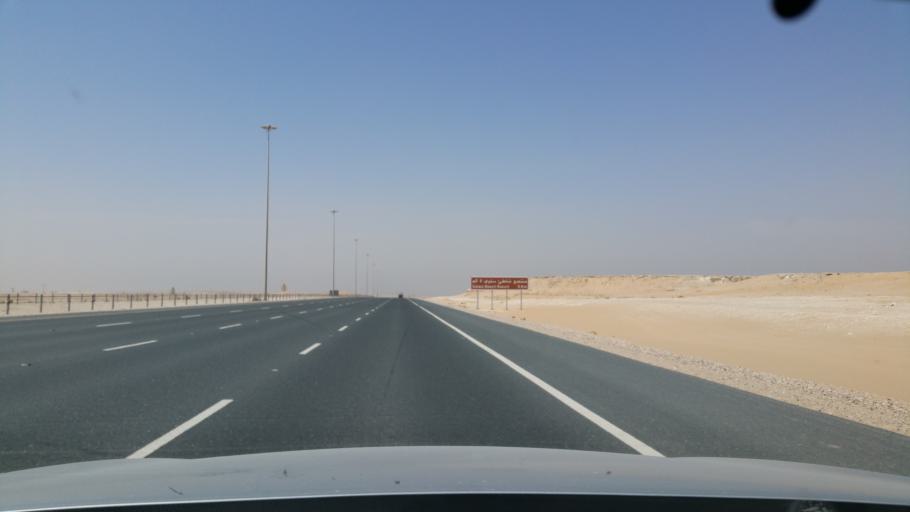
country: QA
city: Umm Bab
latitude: 24.8718
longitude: 50.9148
